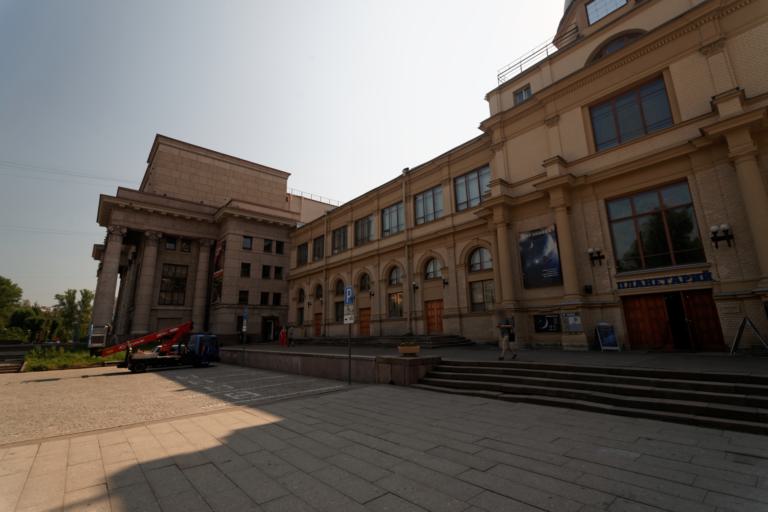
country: RU
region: St.-Petersburg
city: Petrogradka
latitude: 59.9555
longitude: 30.3112
